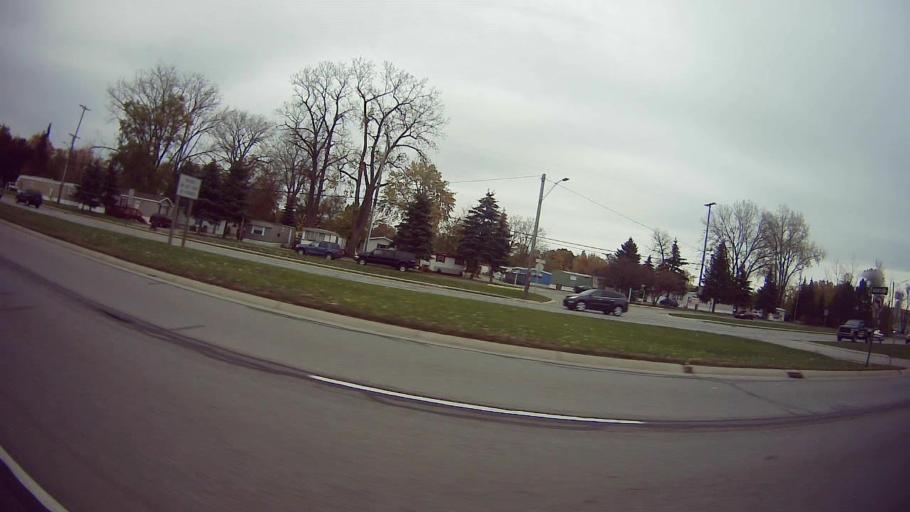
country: US
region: Michigan
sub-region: Oakland County
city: Sylvan Lake
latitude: 42.6233
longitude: -83.3253
